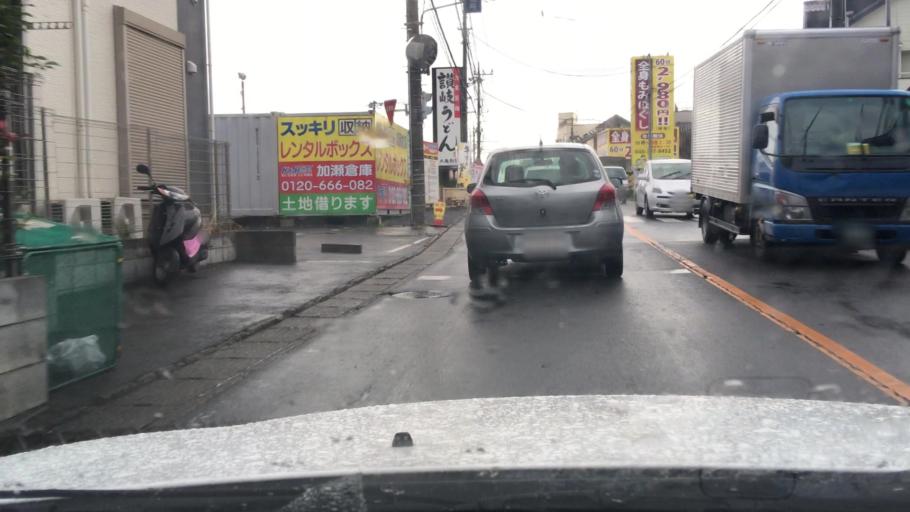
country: JP
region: Saitama
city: Saitama
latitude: 35.9191
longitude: 139.6475
